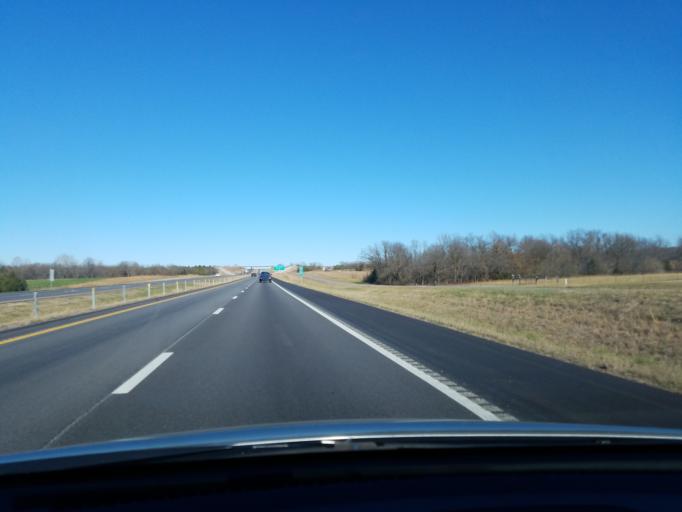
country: US
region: Missouri
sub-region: Webster County
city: Marshfield
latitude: 37.4190
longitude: -92.8850
